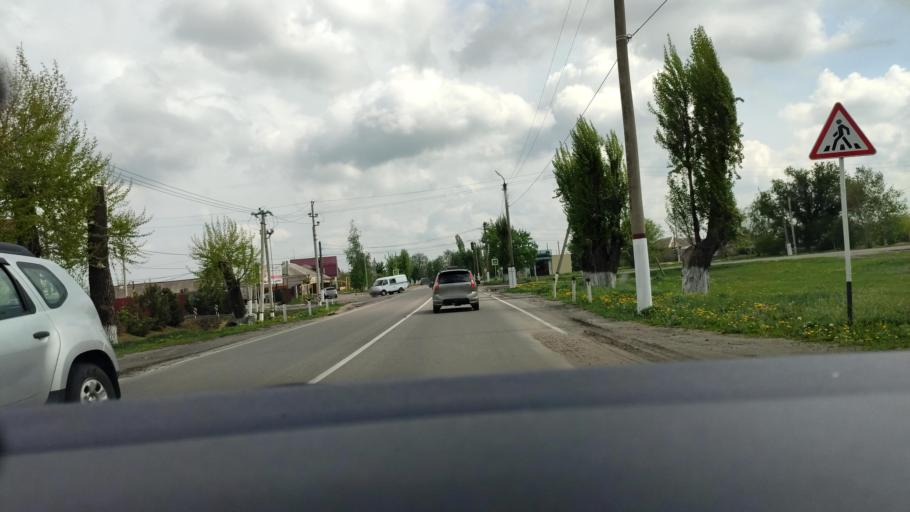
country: RU
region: Voronezj
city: Novaya Usman'
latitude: 51.6144
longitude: 39.3903
